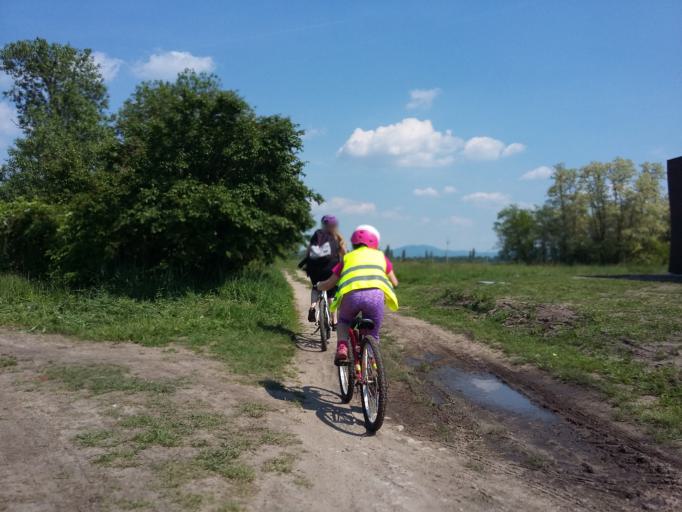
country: SK
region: Bratislavsky
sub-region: Okres Malacky
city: Malacky
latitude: 48.5015
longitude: 16.9797
